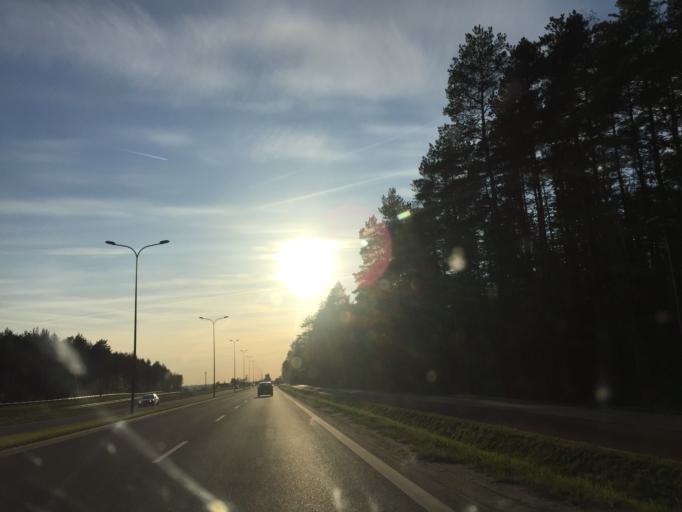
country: PL
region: Pomeranian Voivodeship
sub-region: Sopot
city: Sopot
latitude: 54.3777
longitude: 18.4998
